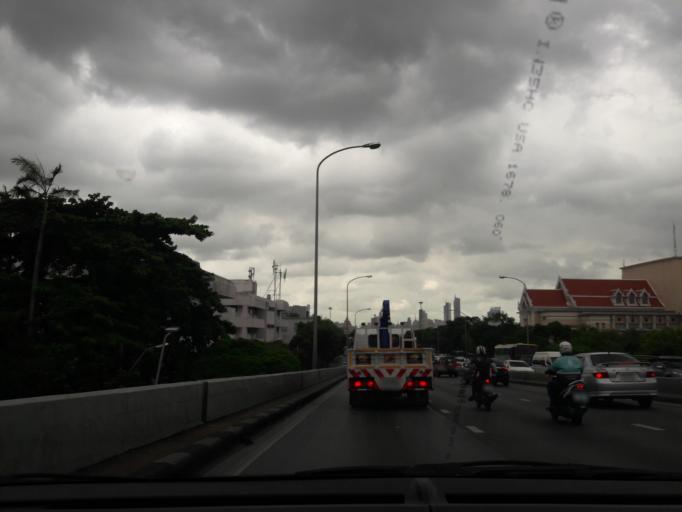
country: TH
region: Bangkok
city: Phra Nakhon
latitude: 13.7609
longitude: 100.4918
